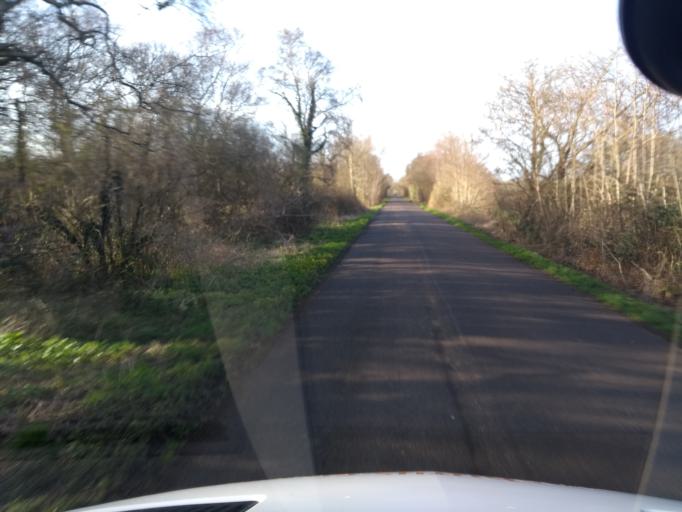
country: GB
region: England
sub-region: Somerset
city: Wedmore
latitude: 51.1627
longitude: -2.8288
